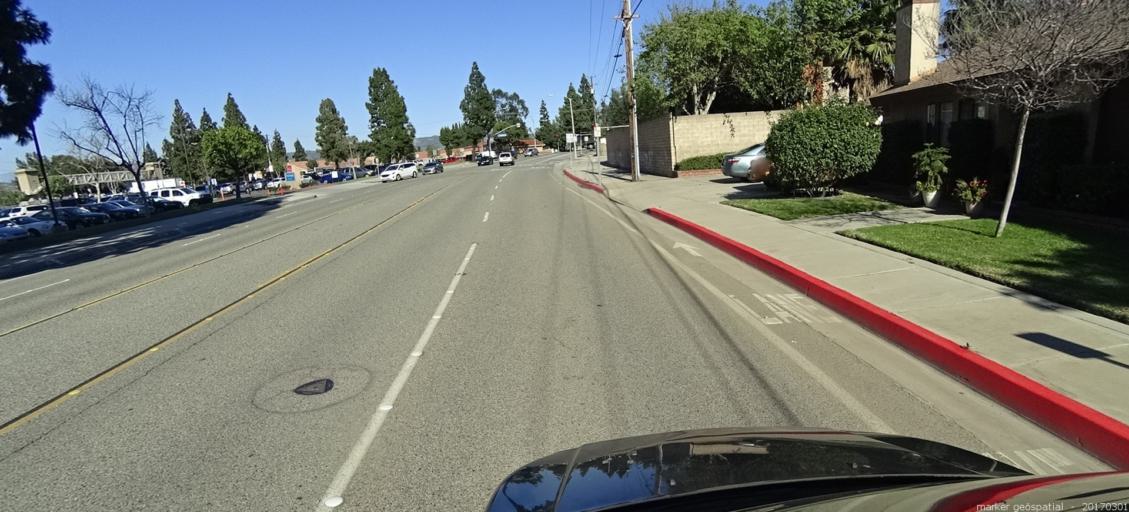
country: US
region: California
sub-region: Orange County
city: Yorba Linda
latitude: 33.8521
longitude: -117.8172
